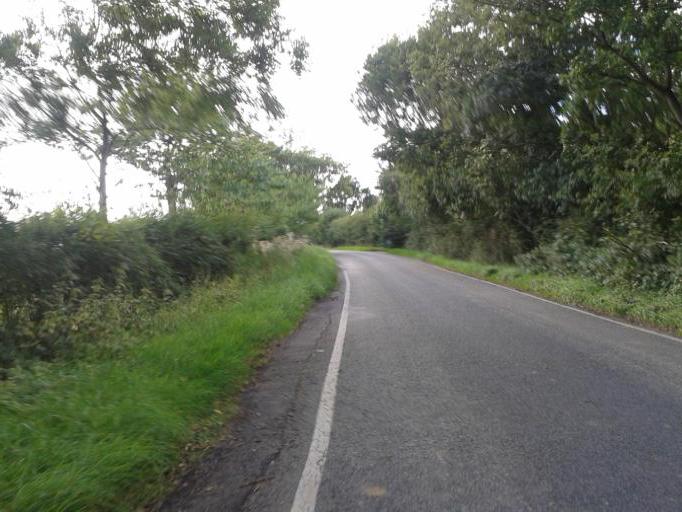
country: GB
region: England
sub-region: Cambridgeshire
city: Duxford
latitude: 52.0042
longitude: 0.1172
